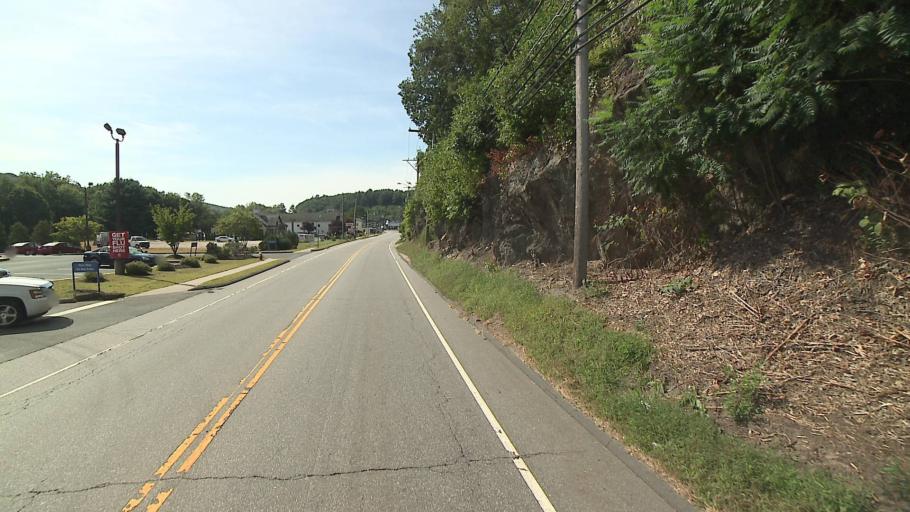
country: US
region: Connecticut
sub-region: Litchfield County
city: Thomaston
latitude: 41.6629
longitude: -73.0797
